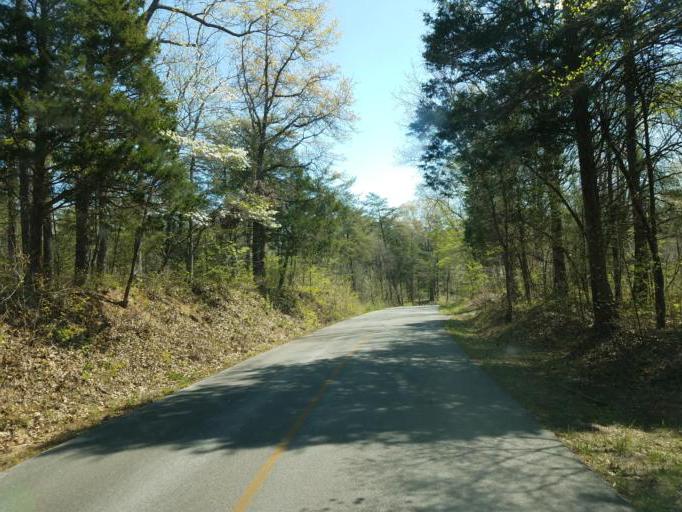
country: US
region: Kentucky
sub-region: Barren County
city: Cave City
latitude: 37.1976
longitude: -86.0658
